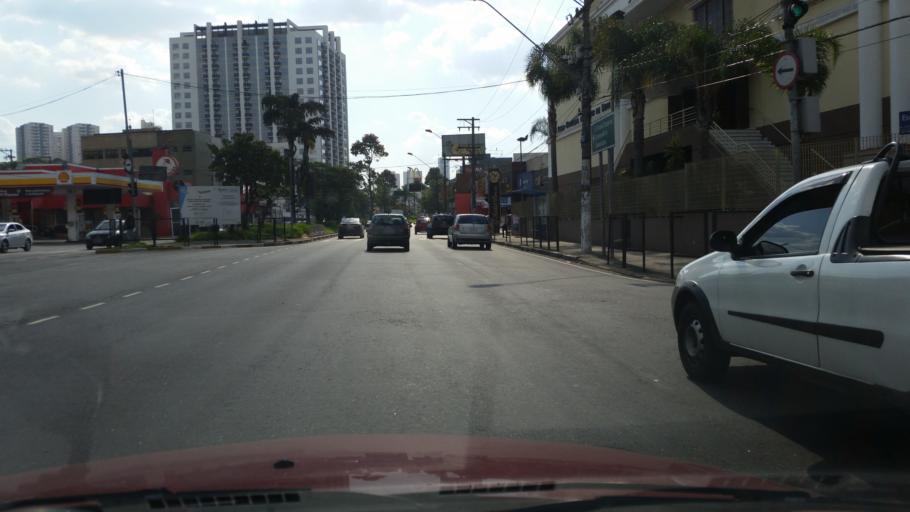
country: BR
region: Sao Paulo
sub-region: Diadema
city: Diadema
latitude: -23.6852
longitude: -46.6170
